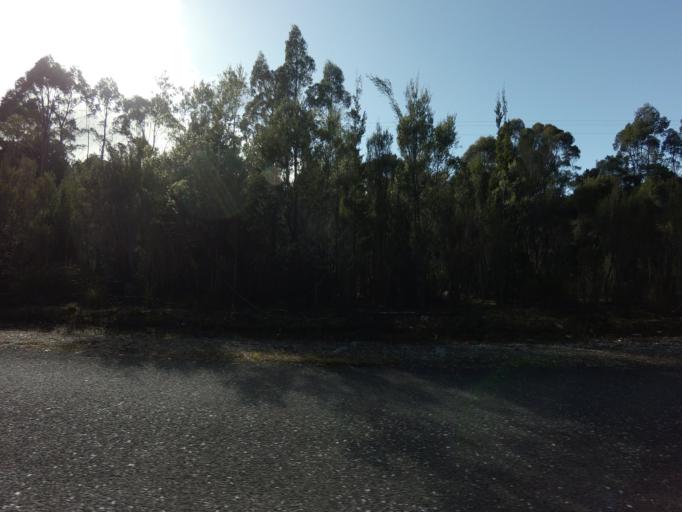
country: AU
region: Tasmania
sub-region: West Coast
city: Queenstown
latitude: -42.7691
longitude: 146.0439
